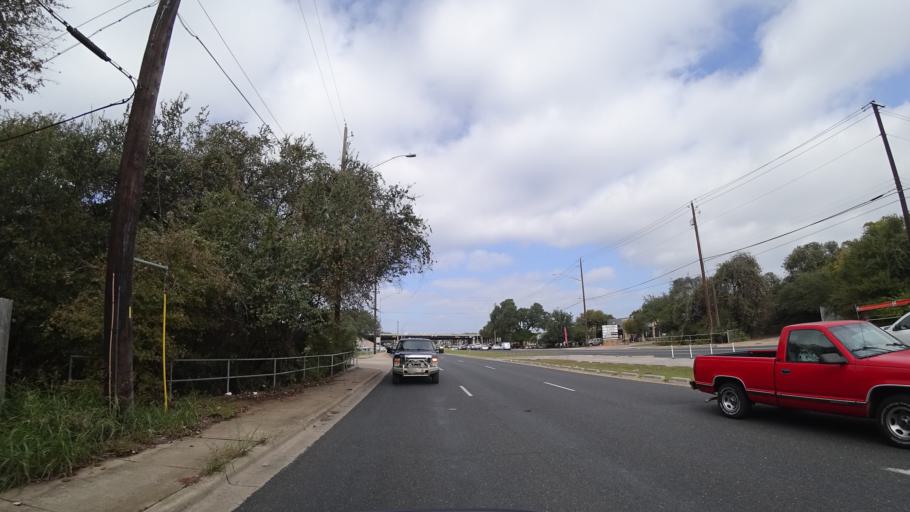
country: US
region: Texas
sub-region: Travis County
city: Shady Hollow
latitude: 30.2185
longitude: -97.8355
